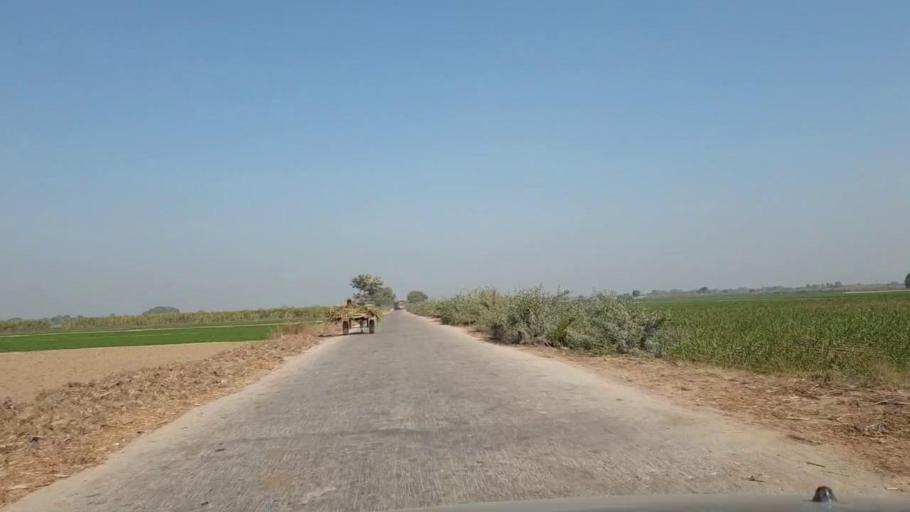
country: PK
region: Sindh
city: Tando Allahyar
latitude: 25.5530
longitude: 68.6081
